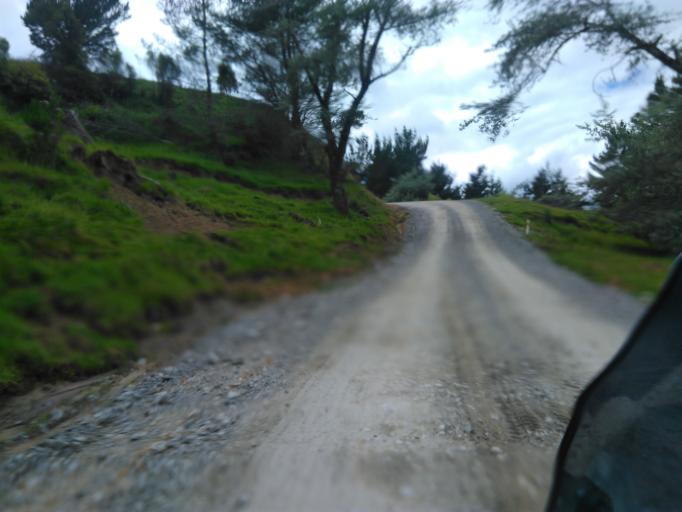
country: NZ
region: Gisborne
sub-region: Gisborne District
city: Gisborne
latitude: -38.0962
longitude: 178.1051
